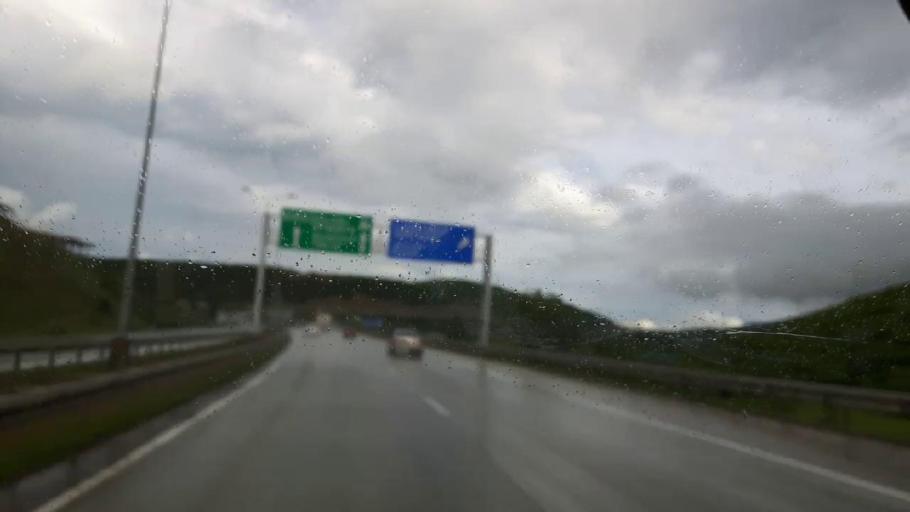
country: GE
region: Shida Kartli
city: Kaspi
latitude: 41.9958
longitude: 44.4122
